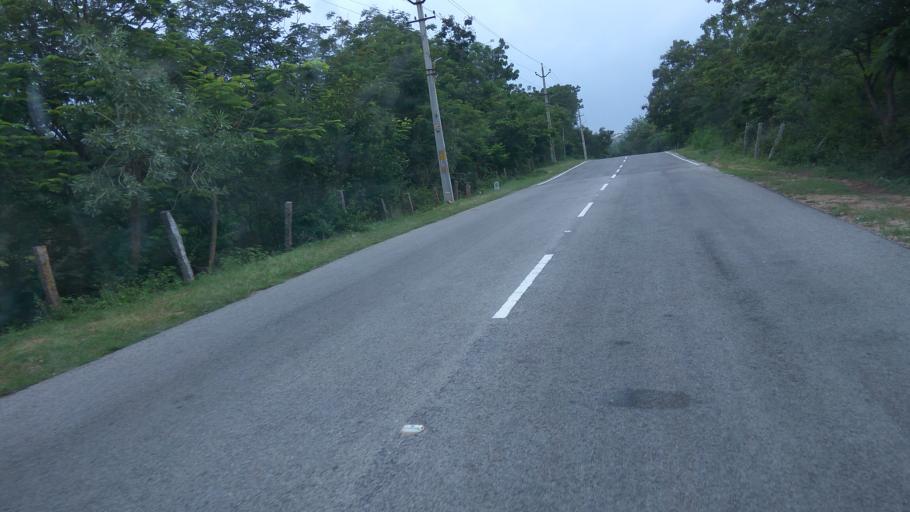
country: IN
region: Telangana
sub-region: Rangareddi
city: Ghatkesar
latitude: 17.5394
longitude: 78.6849
